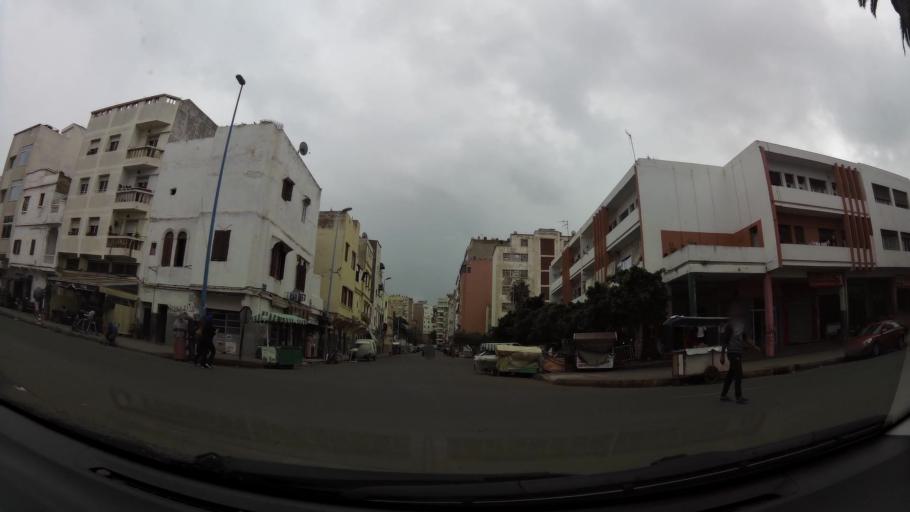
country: MA
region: Grand Casablanca
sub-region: Casablanca
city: Casablanca
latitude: 33.6032
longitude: -7.6350
